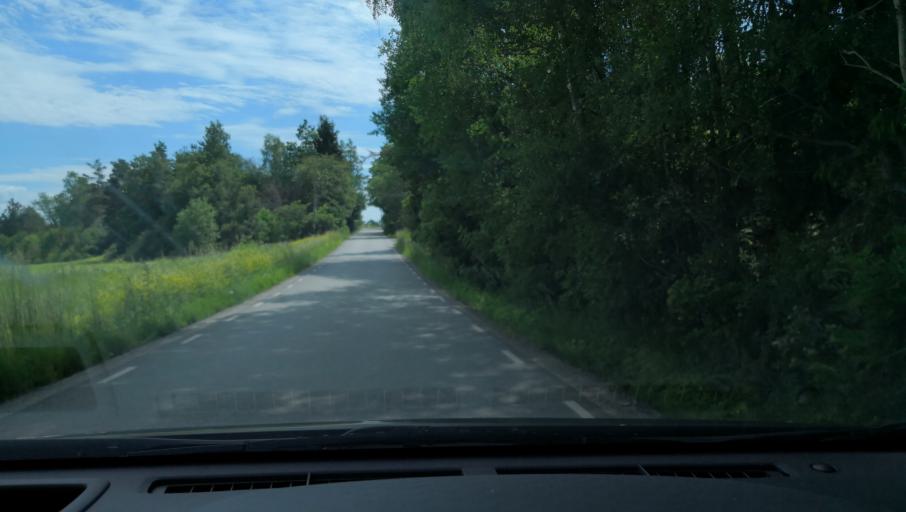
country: SE
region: Uppsala
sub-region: Habo Kommun
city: Balsta
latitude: 59.6818
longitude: 17.4653
